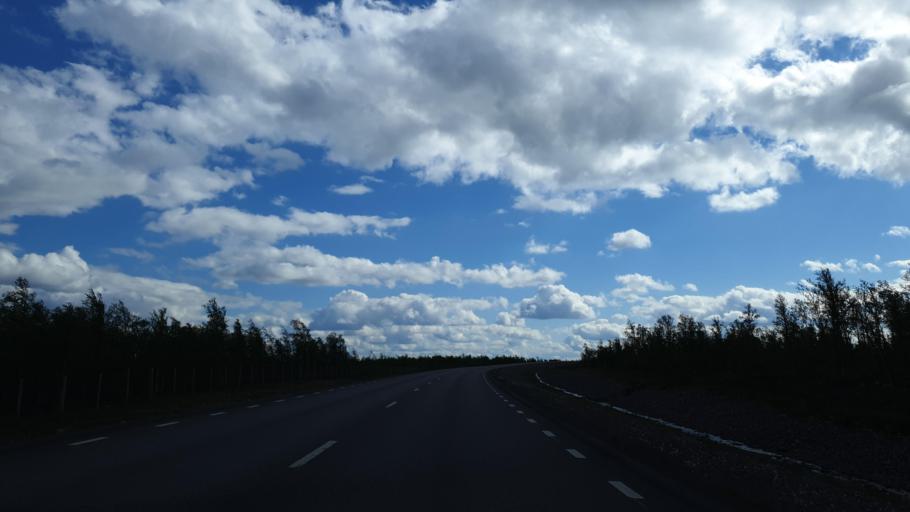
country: SE
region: Norrbotten
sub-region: Kiruna Kommun
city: Kiruna
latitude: 67.8360
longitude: 20.3073
